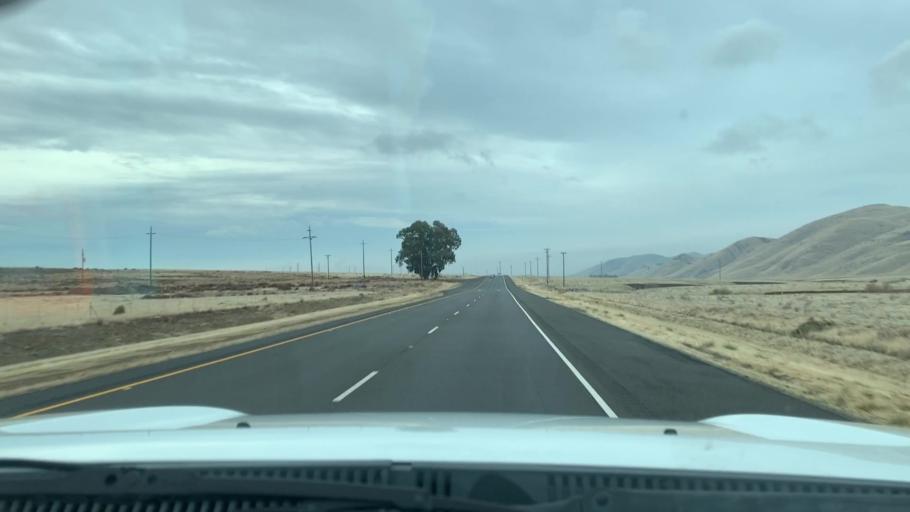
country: US
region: California
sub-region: San Luis Obispo County
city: Shandon
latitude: 35.7128
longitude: -120.1681
